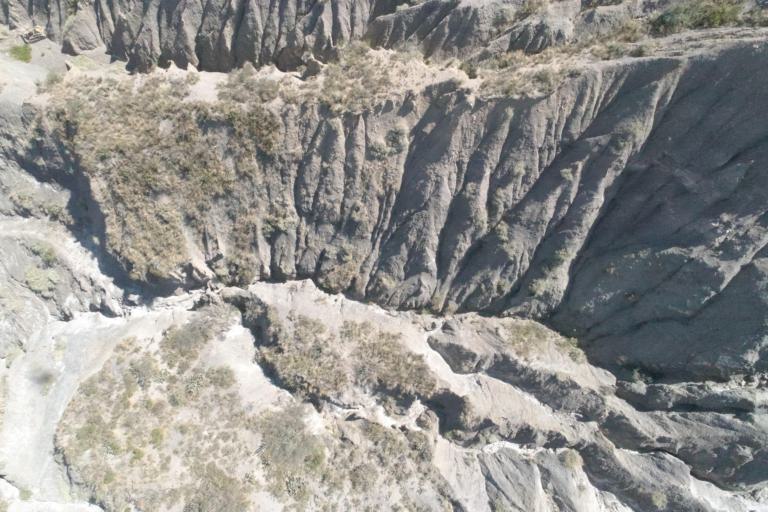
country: BO
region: La Paz
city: La Paz
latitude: -16.6234
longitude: -68.0396
